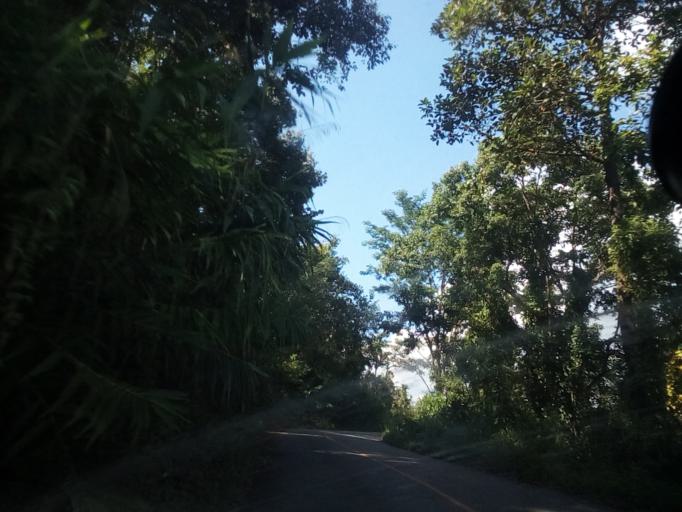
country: TH
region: Chiang Mai
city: Samoeng
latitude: 18.8625
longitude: 98.6970
